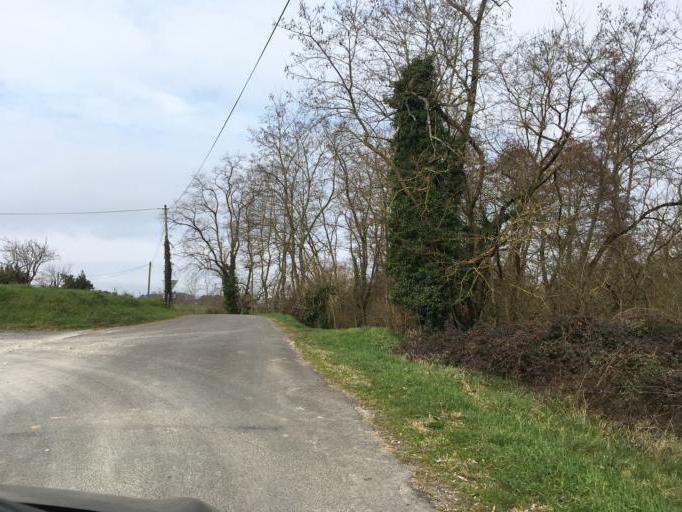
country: FR
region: Poitou-Charentes
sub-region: Departement de la Charente-Maritime
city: Mirambeau
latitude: 45.3266
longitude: -0.5779
